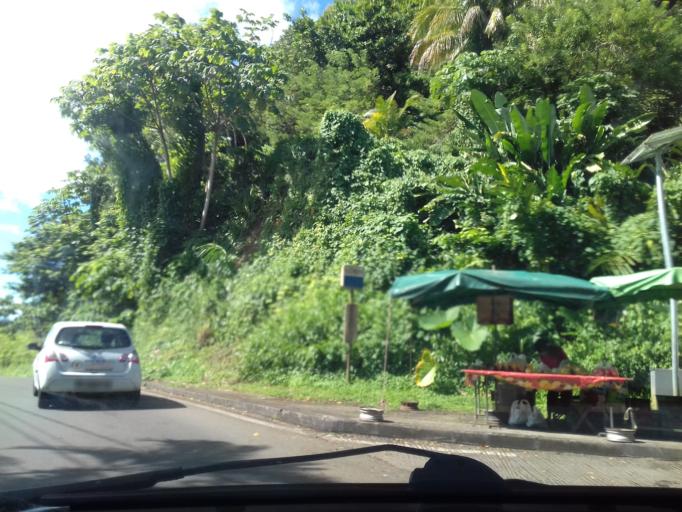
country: MQ
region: Martinique
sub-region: Martinique
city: Saint-Joseph
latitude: 14.6714
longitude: -61.0460
